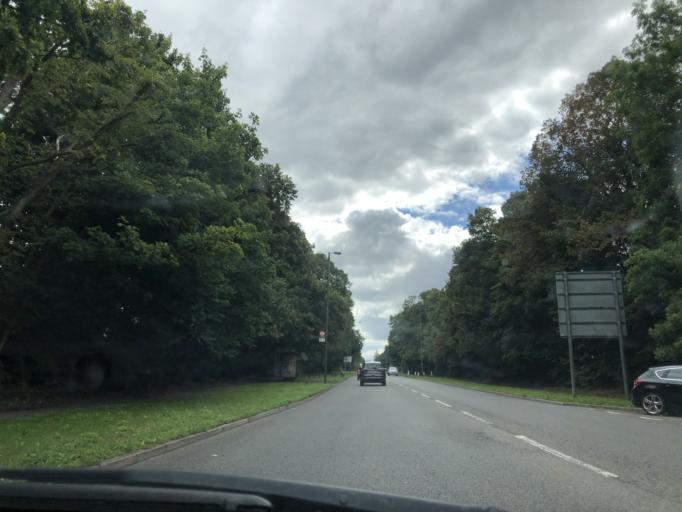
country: GB
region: England
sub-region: Greater London
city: Orpington
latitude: 51.3701
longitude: 0.1096
